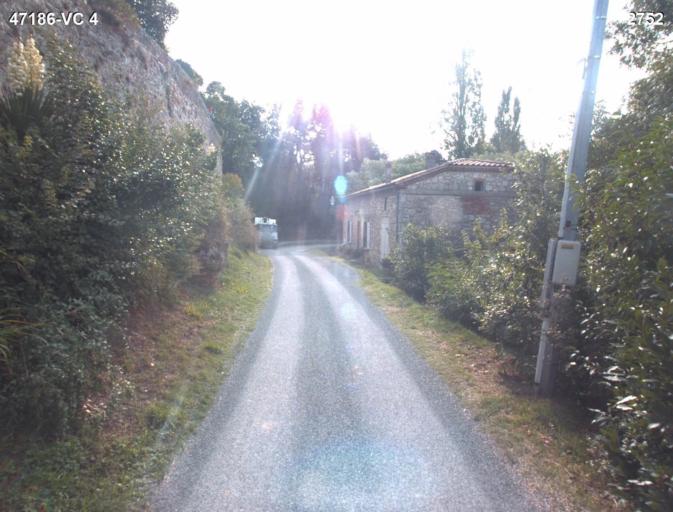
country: FR
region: Aquitaine
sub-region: Departement du Lot-et-Garonne
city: Port-Sainte-Marie
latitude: 44.2016
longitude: 0.4411
